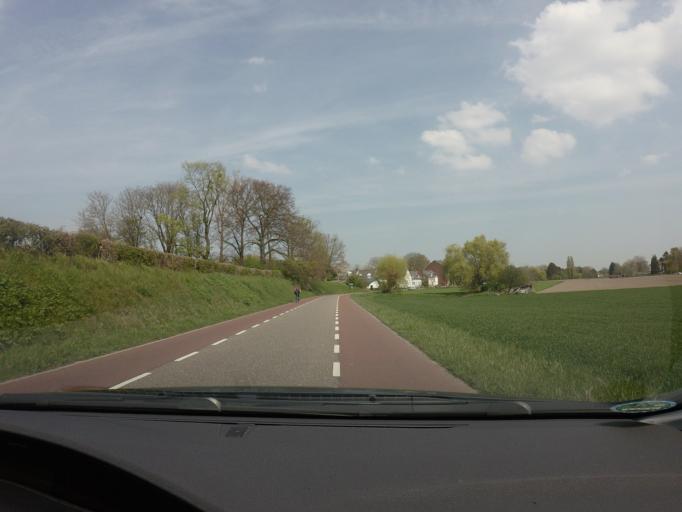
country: NL
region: Limburg
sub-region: Gemeente Maastricht
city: Maastricht
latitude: 50.8336
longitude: 5.6699
